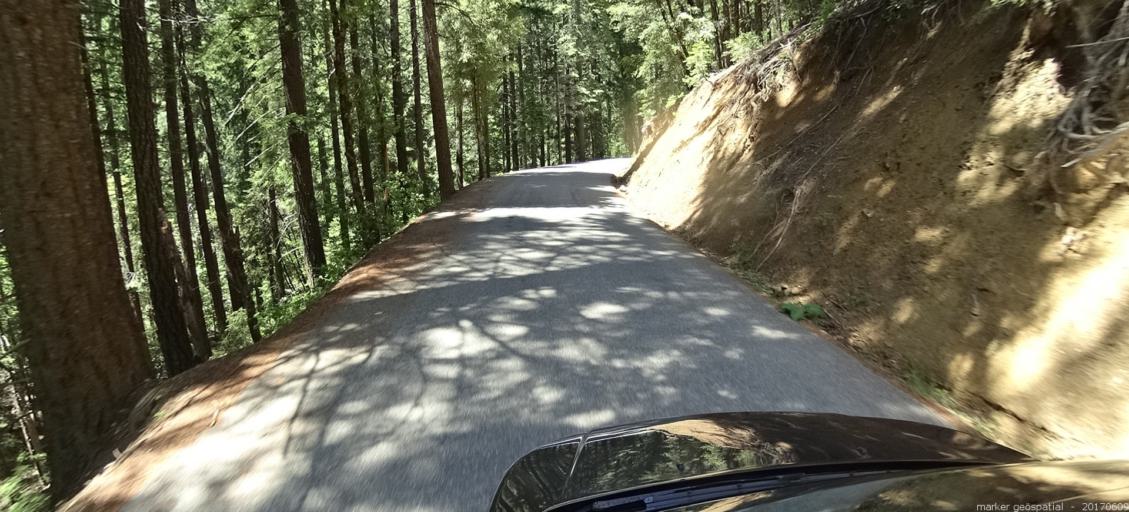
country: US
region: California
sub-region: Siskiyou County
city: Yreka
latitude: 41.3774
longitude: -123.0190
